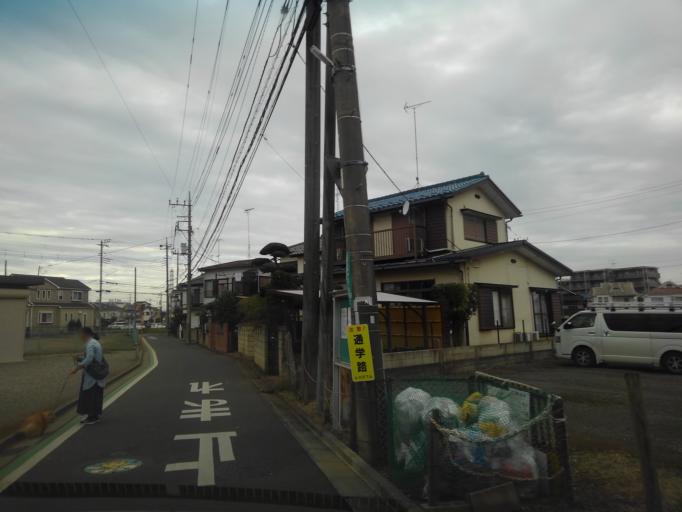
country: JP
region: Saitama
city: Tokorozawa
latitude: 35.7975
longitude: 139.4499
